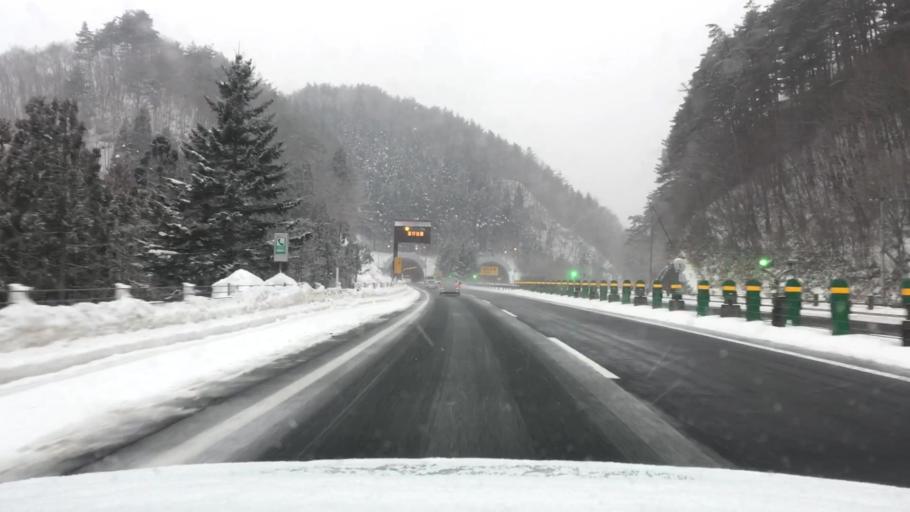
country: JP
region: Akita
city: Hanawa
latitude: 40.1167
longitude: 141.0271
